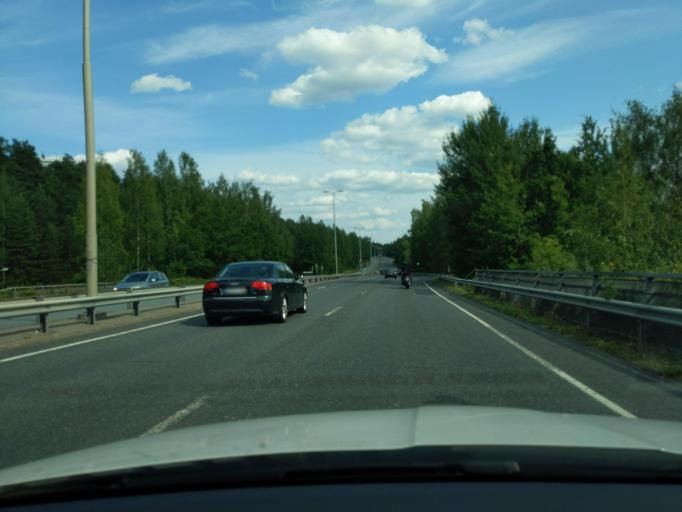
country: FI
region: Paijanne Tavastia
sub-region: Lahti
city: Lahti
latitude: 60.9751
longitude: 25.6891
